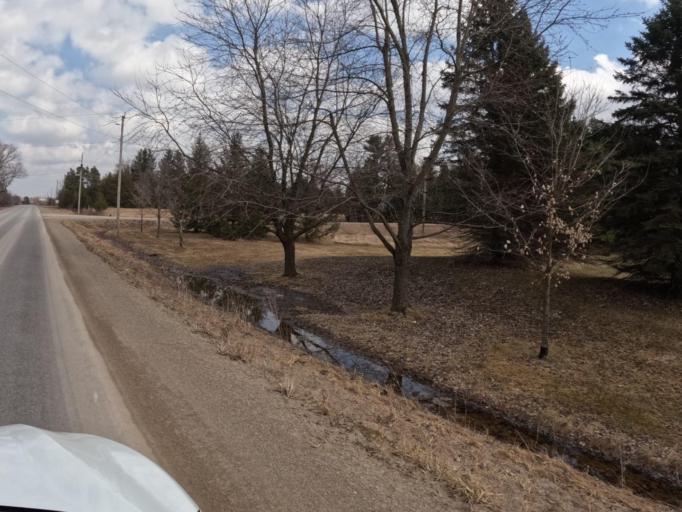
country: CA
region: Ontario
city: Shelburne
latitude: 44.0028
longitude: -80.2373
